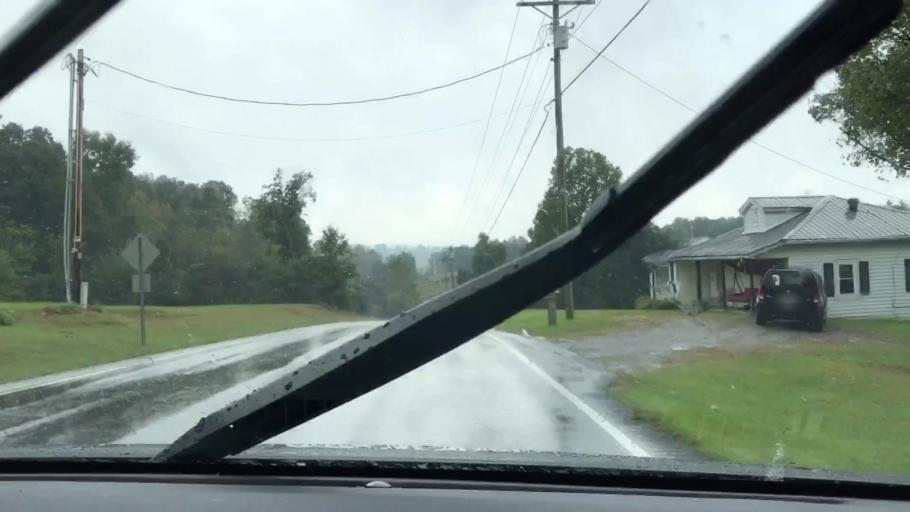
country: US
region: Kentucky
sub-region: Monroe County
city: Tompkinsville
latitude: 36.6549
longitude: -85.7444
